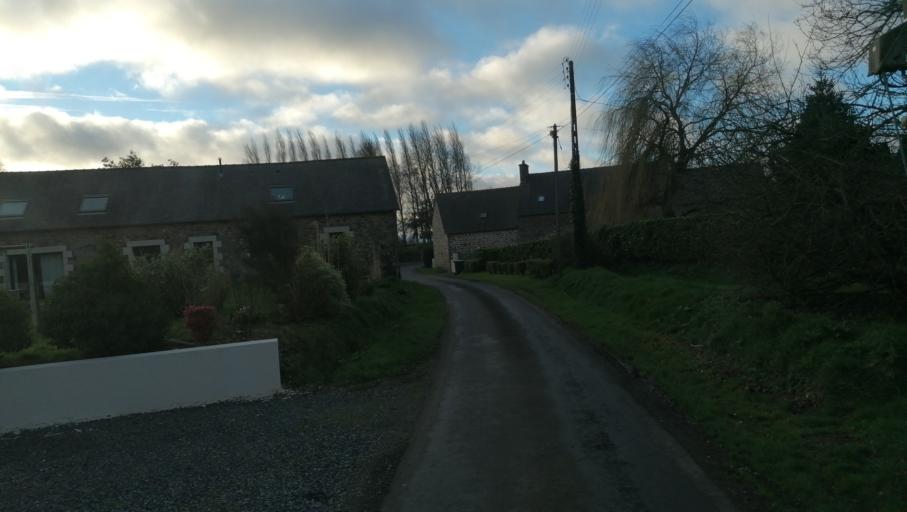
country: FR
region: Brittany
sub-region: Departement des Cotes-d'Armor
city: Pommerit-le-Vicomte
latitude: 48.6415
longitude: -3.0598
